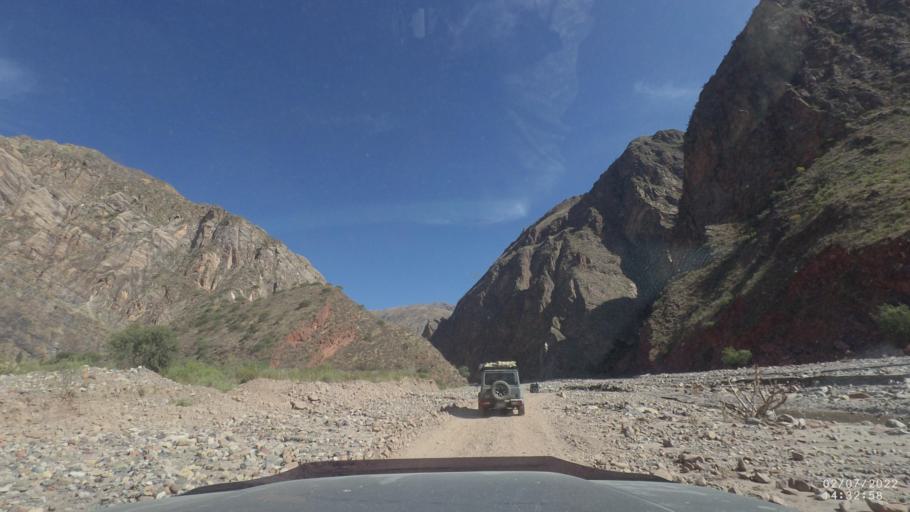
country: BO
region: Cochabamba
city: Irpa Irpa
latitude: -17.8372
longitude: -66.4149
